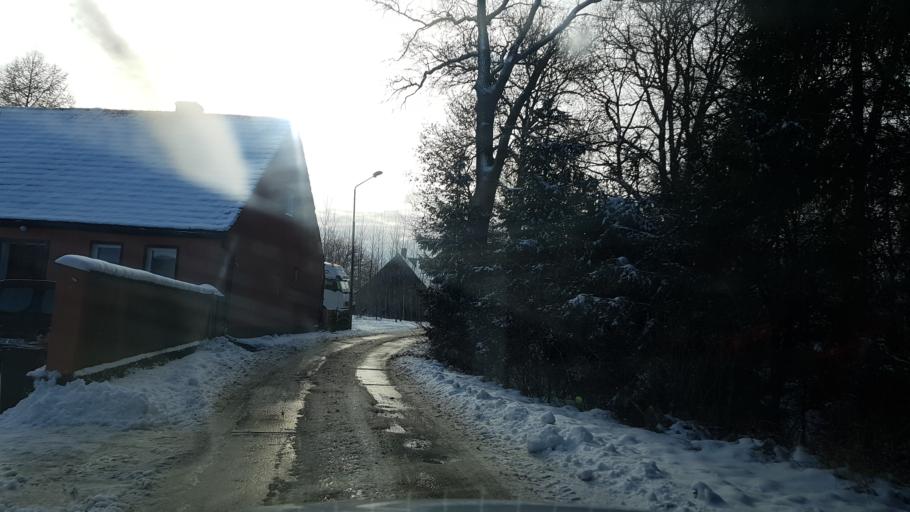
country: PL
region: West Pomeranian Voivodeship
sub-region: Powiat drawski
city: Drawsko Pomorskie
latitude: 53.5402
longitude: 15.7872
